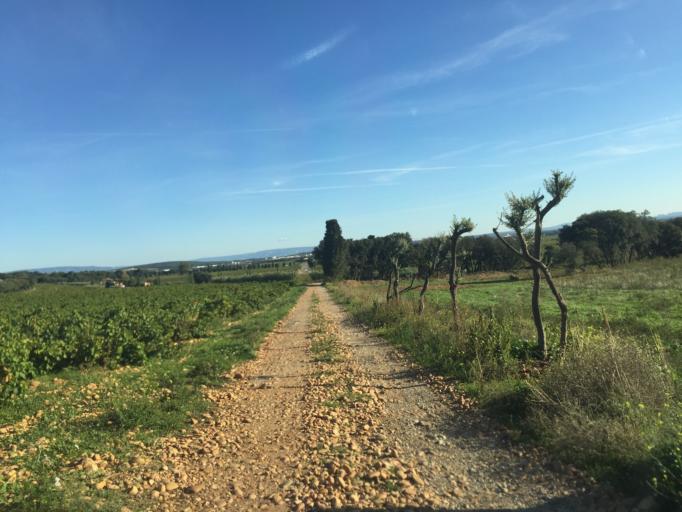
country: FR
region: Provence-Alpes-Cote d'Azur
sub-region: Departement du Vaucluse
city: Chateauneuf-du-Pape
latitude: 44.0506
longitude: 4.8396
